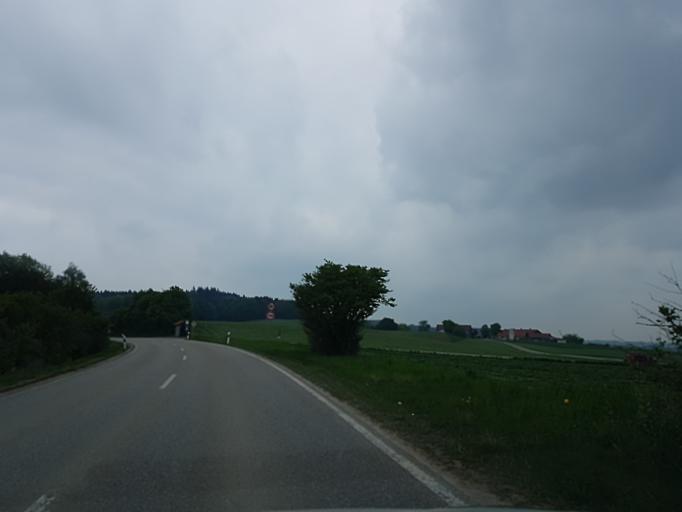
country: DE
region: Bavaria
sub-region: Upper Bavaria
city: Ebersberg
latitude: 48.0926
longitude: 11.9743
